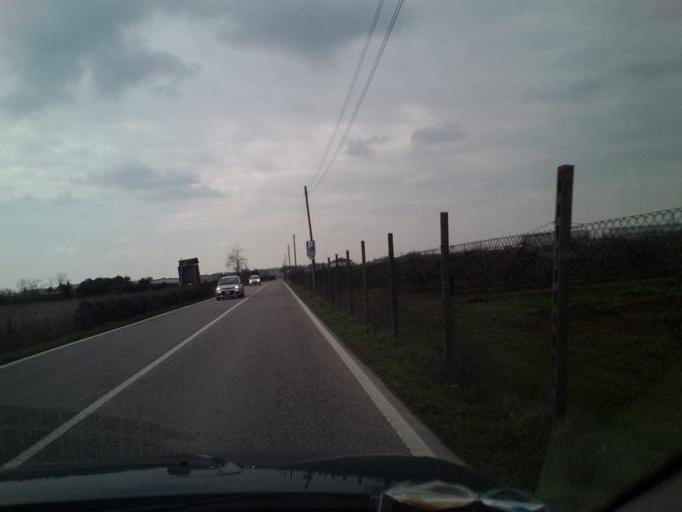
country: IT
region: Veneto
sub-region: Provincia di Verona
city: Caselle
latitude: 45.4089
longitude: 10.8754
